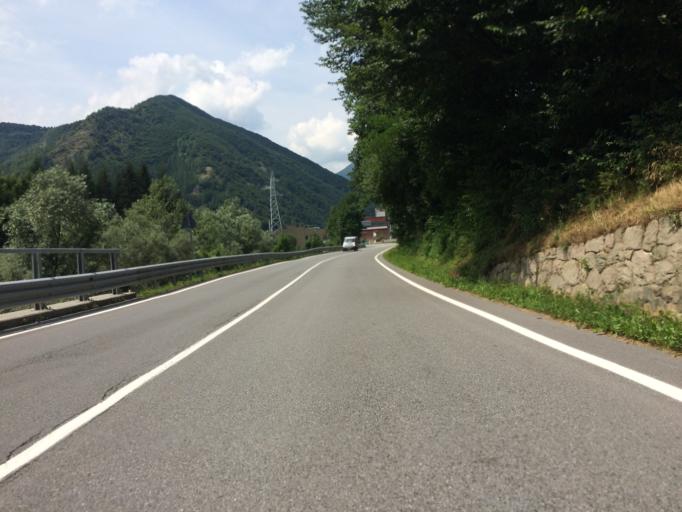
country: IT
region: Piedmont
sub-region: Provincia di Cuneo
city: Vernante
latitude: 44.2390
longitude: 7.5405
